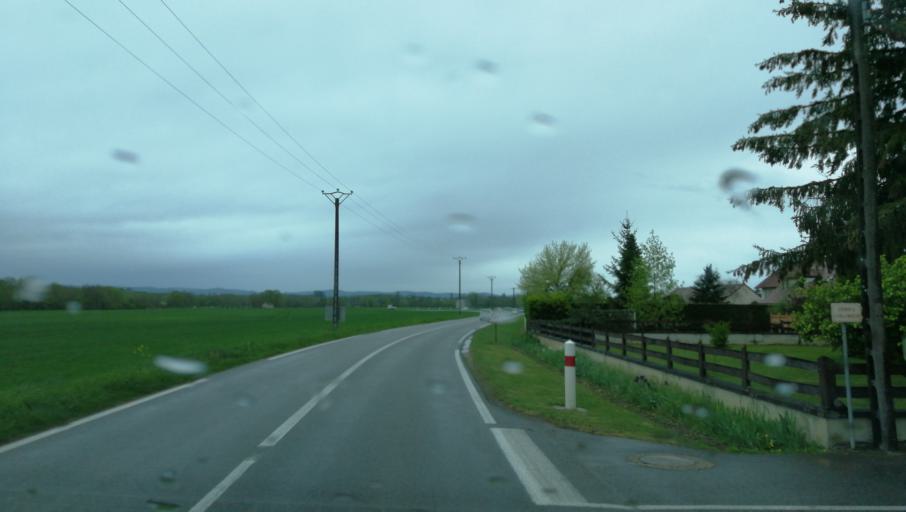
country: FR
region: Franche-Comte
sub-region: Departement du Jura
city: Bletterans
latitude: 46.7341
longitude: 5.4697
